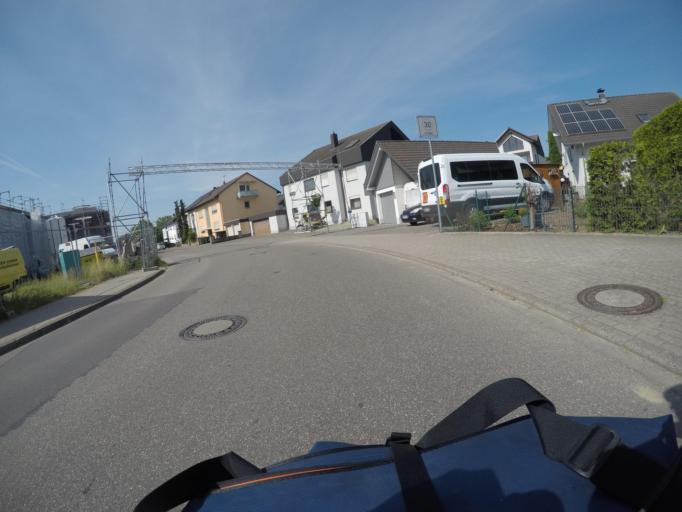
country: DE
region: Baden-Wuerttemberg
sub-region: Karlsruhe Region
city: Bietigheim
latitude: 48.9033
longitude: 8.2498
